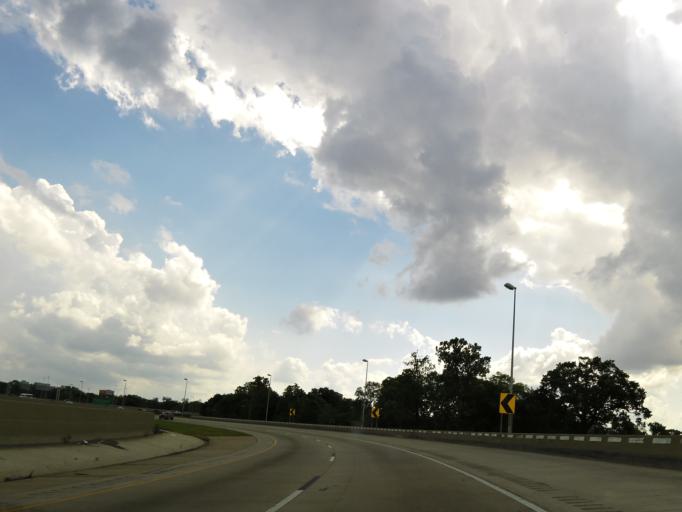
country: US
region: Alabama
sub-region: Jefferson County
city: Tarrant
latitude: 33.5479
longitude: -86.7516
